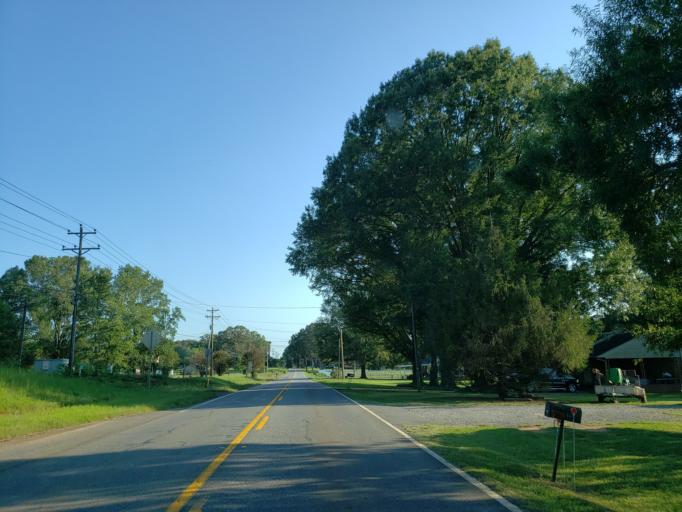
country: US
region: Georgia
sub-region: Murray County
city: Chatsworth
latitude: 34.7805
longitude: -84.8243
